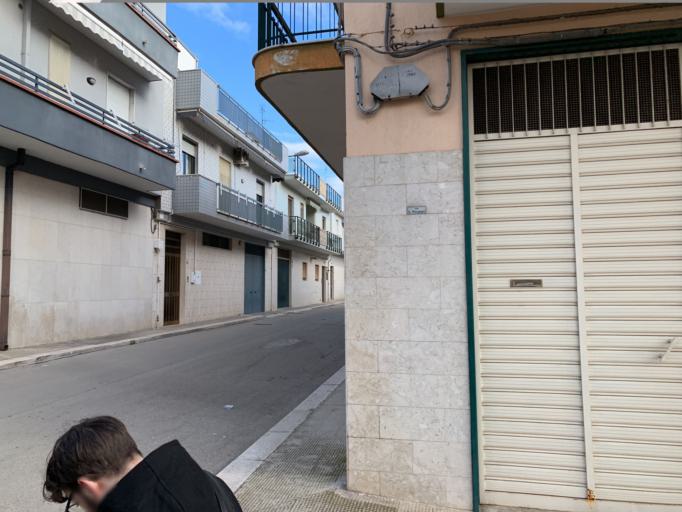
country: IT
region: Apulia
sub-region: Provincia di Barletta - Andria - Trani
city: Andria
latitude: 41.2311
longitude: 16.2851
